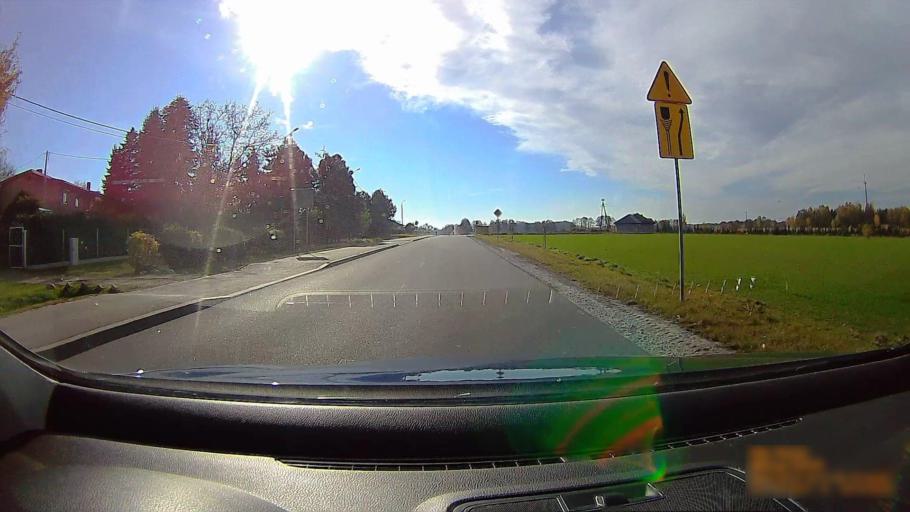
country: PL
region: Greater Poland Voivodeship
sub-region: Powiat ostrzeszowski
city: Doruchow
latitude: 51.3582
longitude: 18.0303
